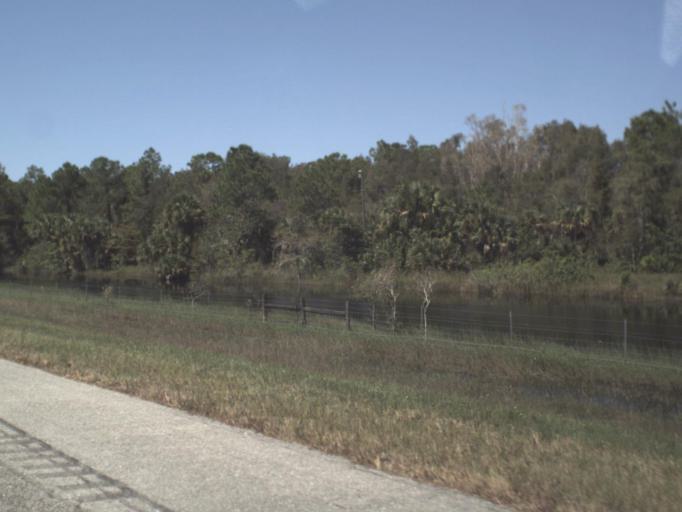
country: US
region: Florida
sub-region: Collier County
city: Golden Gate
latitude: 26.1543
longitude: -81.6117
